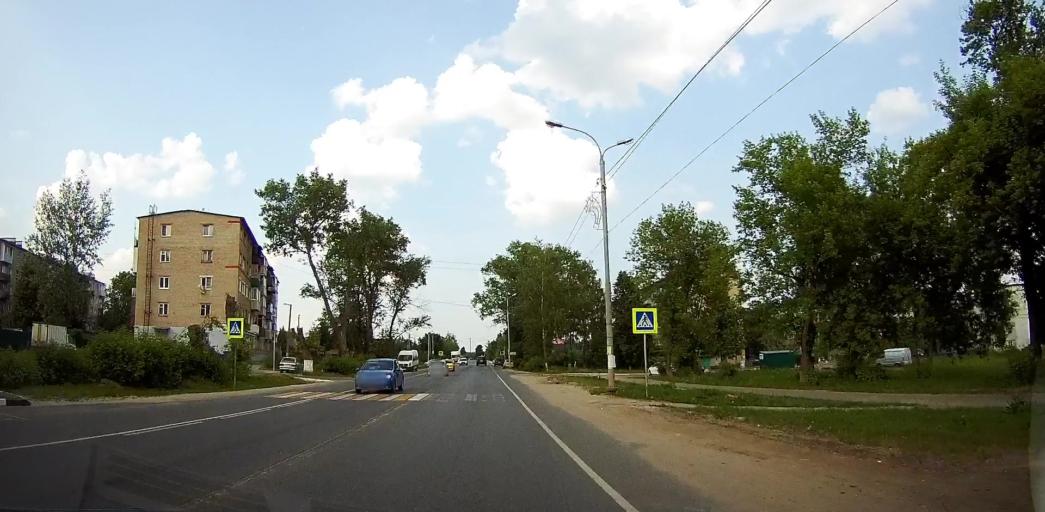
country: RU
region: Moskovskaya
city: Mikhnevo
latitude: 55.1274
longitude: 37.9467
